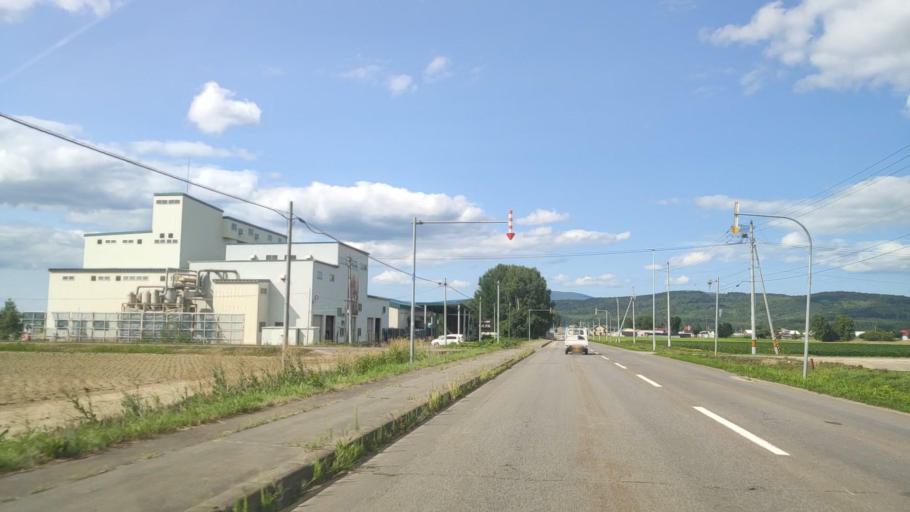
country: JP
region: Hokkaido
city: Nayoro
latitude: 44.4317
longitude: 142.4012
